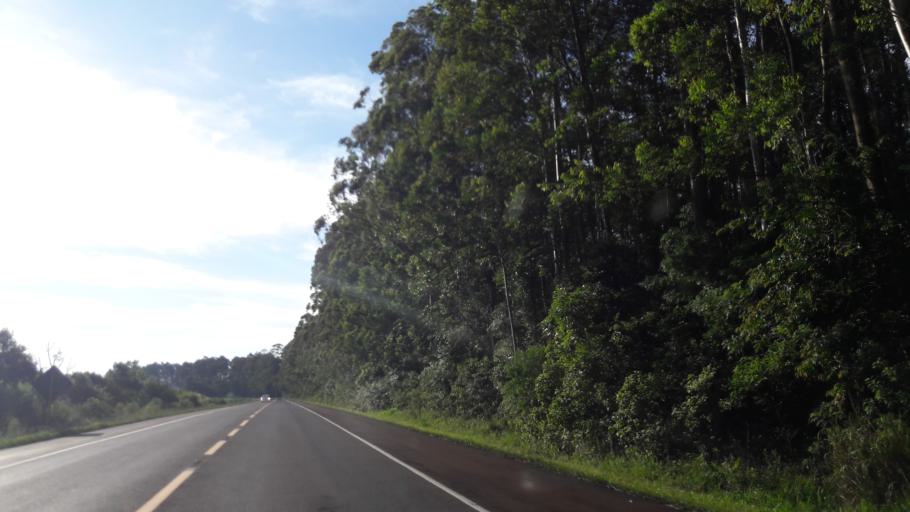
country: BR
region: Parana
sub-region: Campo Mourao
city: Campo Mourao
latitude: -24.2876
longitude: -52.5653
